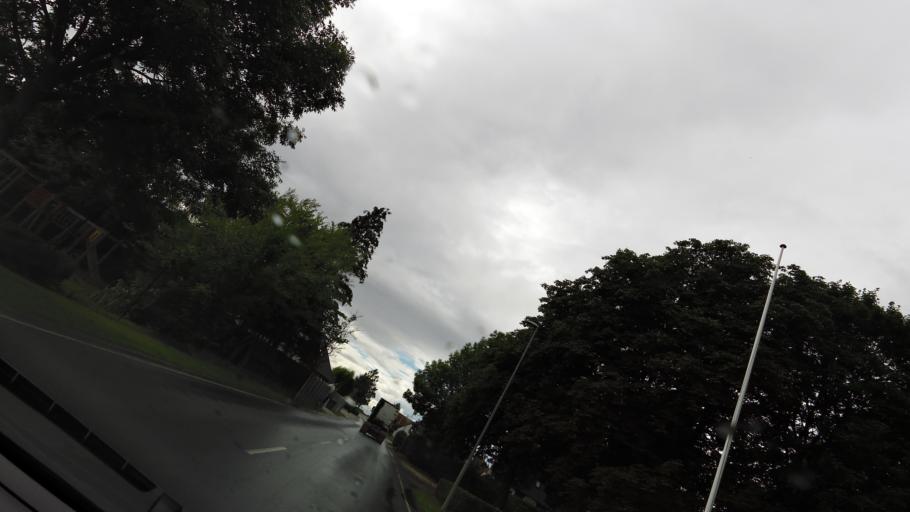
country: DK
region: South Denmark
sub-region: Nordfyns Kommune
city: Otterup
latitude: 55.4872
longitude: 10.3441
